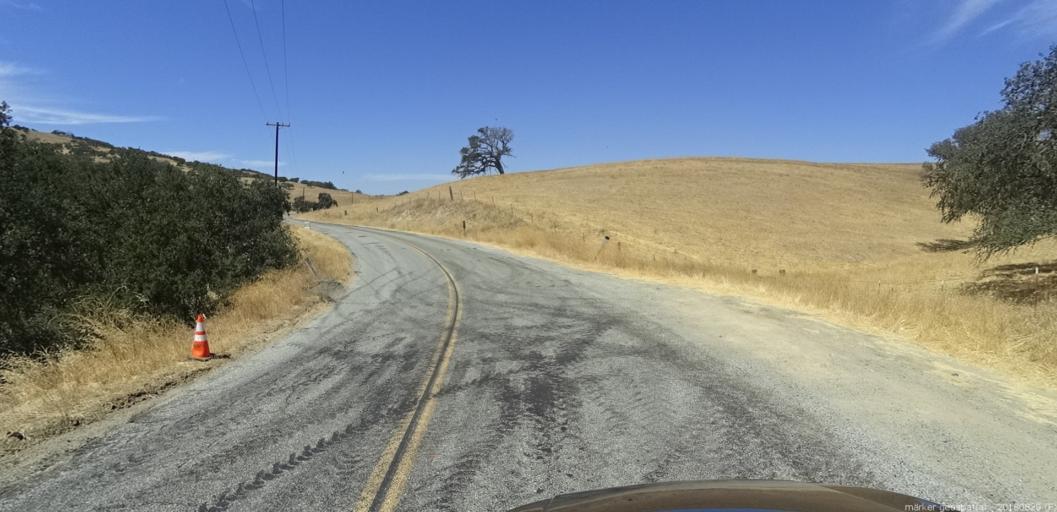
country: US
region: California
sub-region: San Luis Obispo County
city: Lake Nacimiento
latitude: 35.8255
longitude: -120.8424
